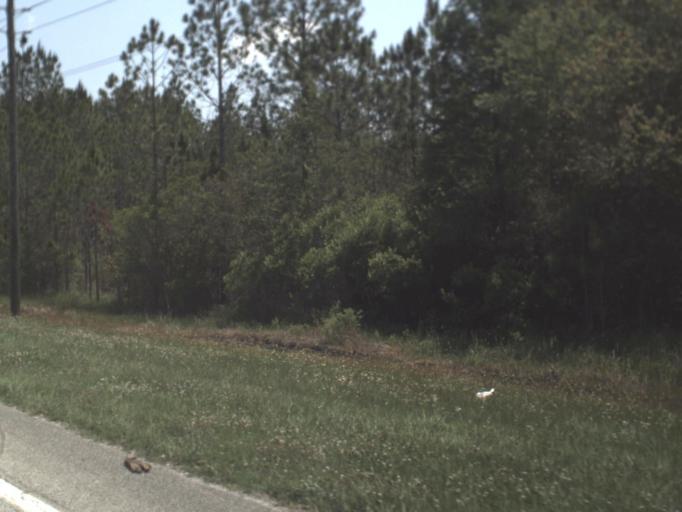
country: US
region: Florida
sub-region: Duval County
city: Baldwin
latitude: 30.2277
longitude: -82.0045
